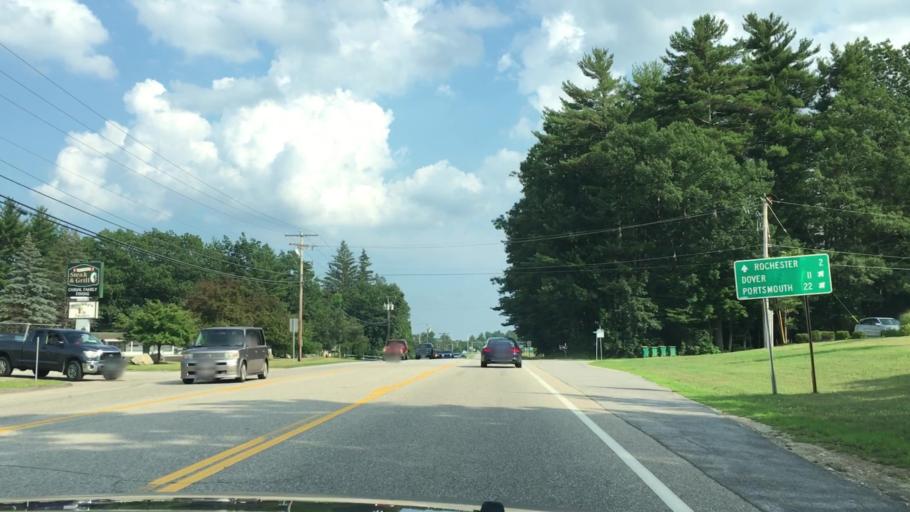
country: US
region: New Hampshire
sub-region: Strafford County
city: Rochester
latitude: 43.3231
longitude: -70.9999
